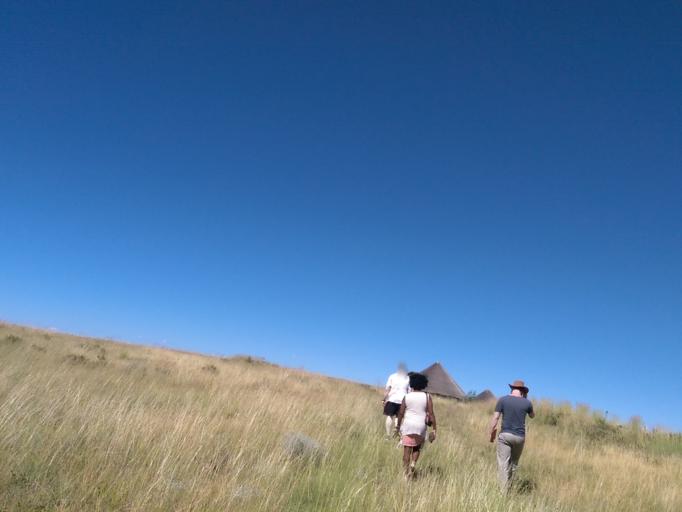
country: LS
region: Maseru
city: Maseru
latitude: -29.4828
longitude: 27.5824
